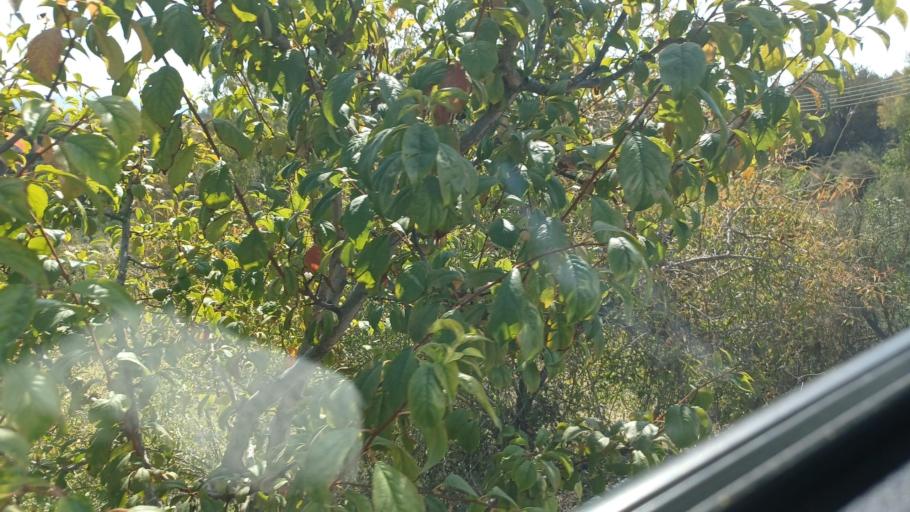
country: CY
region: Pafos
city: Tala
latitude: 34.8650
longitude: 32.4761
